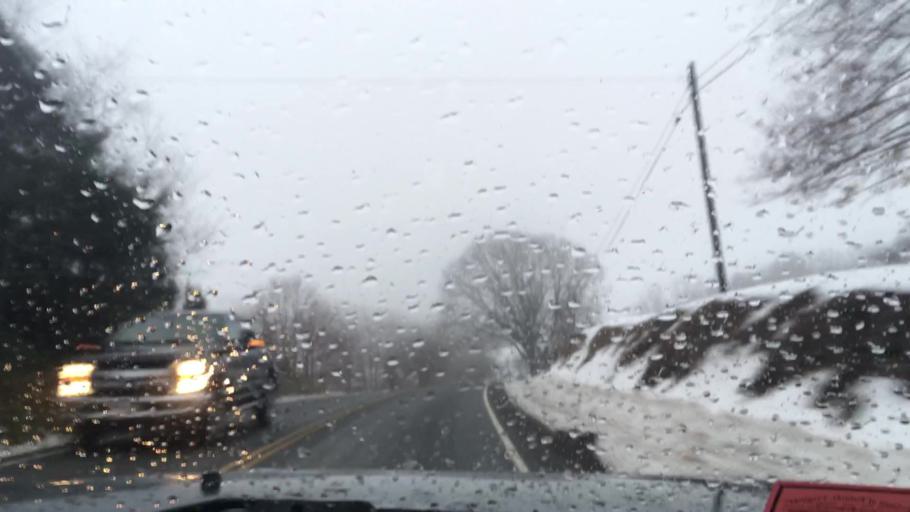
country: US
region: Virginia
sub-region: Pulaski County
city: Pulaski
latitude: 37.0267
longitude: -80.7160
